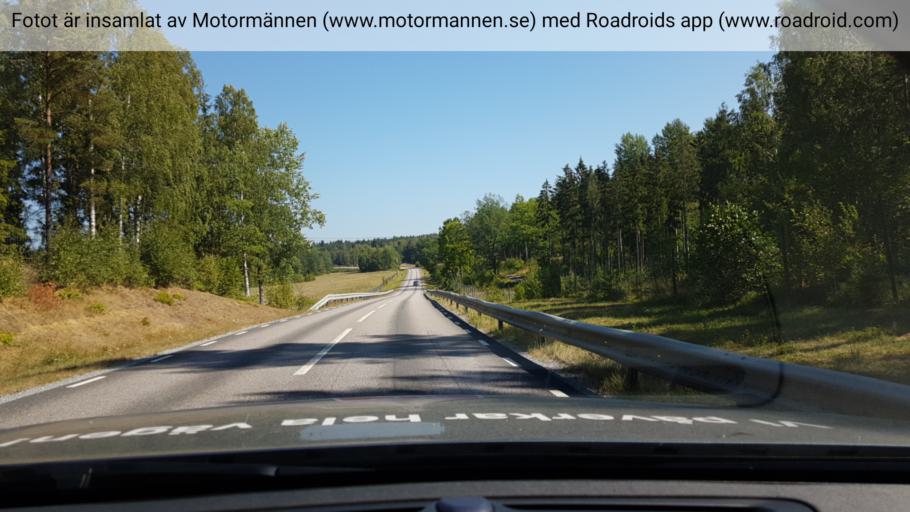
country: SE
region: Stockholm
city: Stenhamra
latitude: 59.3274
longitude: 17.6351
